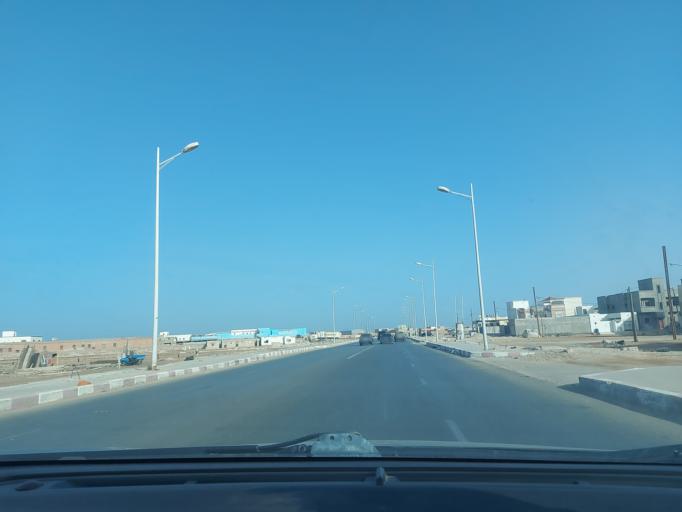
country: MR
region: Nouakchott
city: Nouakchott
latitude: 18.0963
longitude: -16.0174
